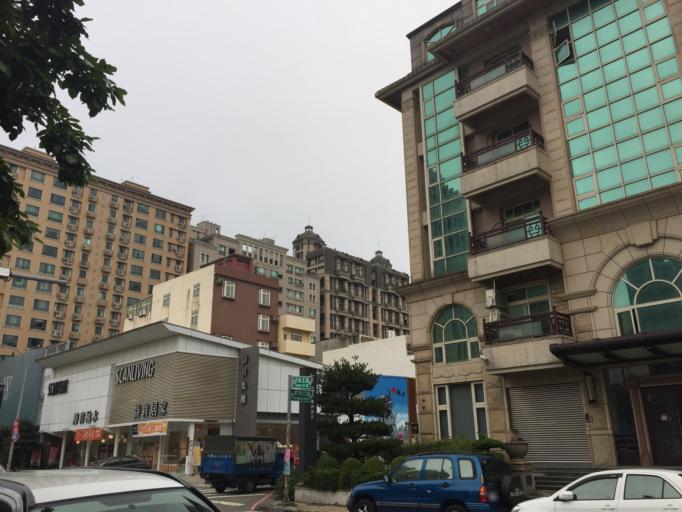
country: TW
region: Taiwan
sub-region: Hsinchu
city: Zhubei
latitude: 24.8196
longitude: 121.0238
